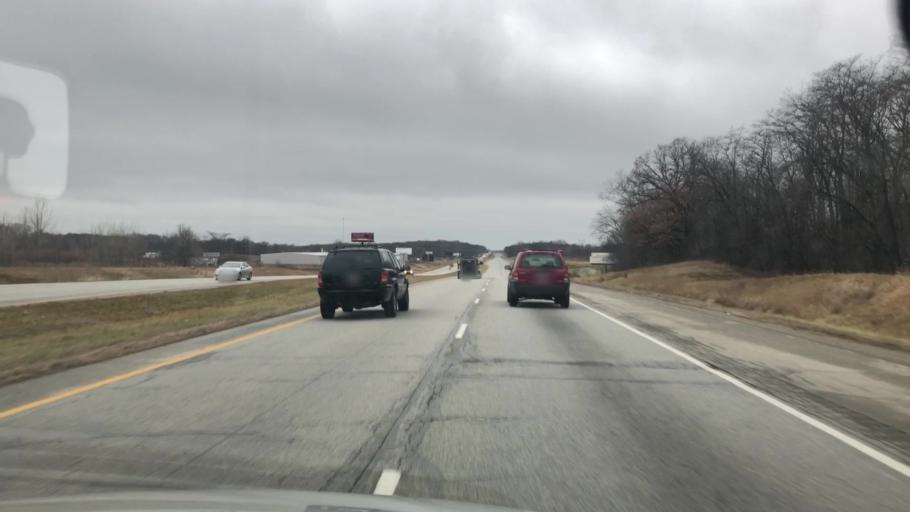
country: US
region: Indiana
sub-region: Kosciusko County
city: Warsaw
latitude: 41.2703
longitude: -85.8738
